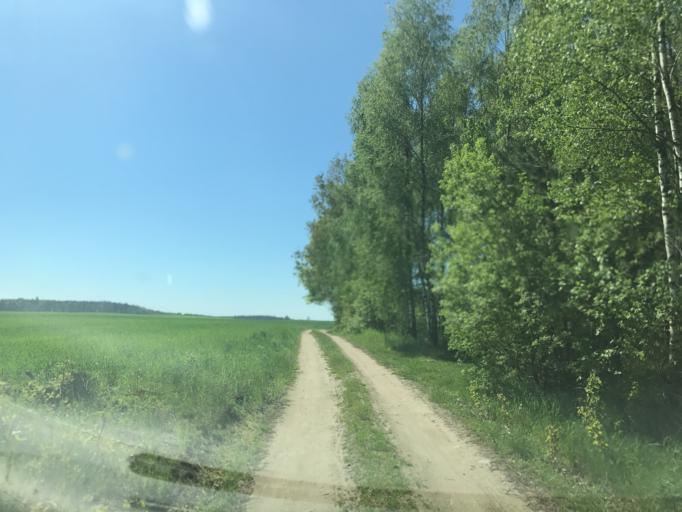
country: PL
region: Warmian-Masurian Voivodeship
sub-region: Powiat dzialdowski
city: Lidzbark
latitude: 53.2447
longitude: 19.7627
